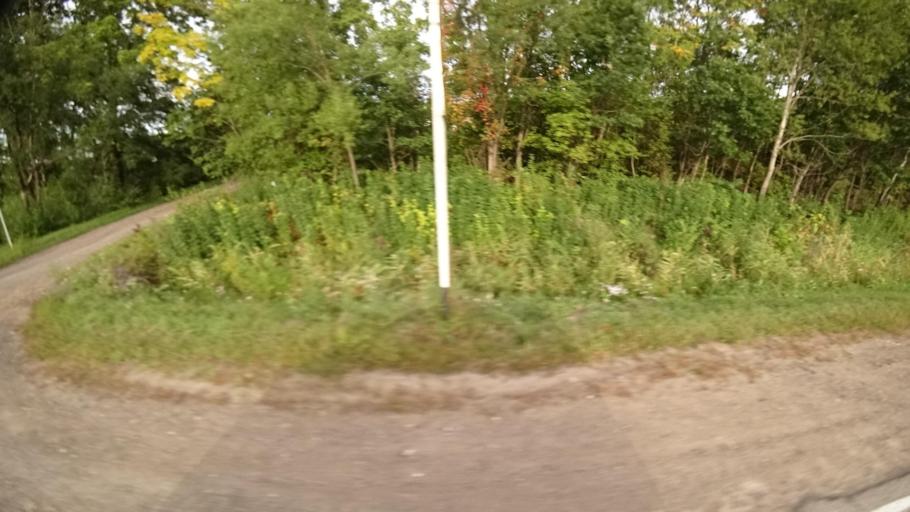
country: RU
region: Primorskiy
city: Yakovlevka
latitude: 44.4146
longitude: 133.4534
